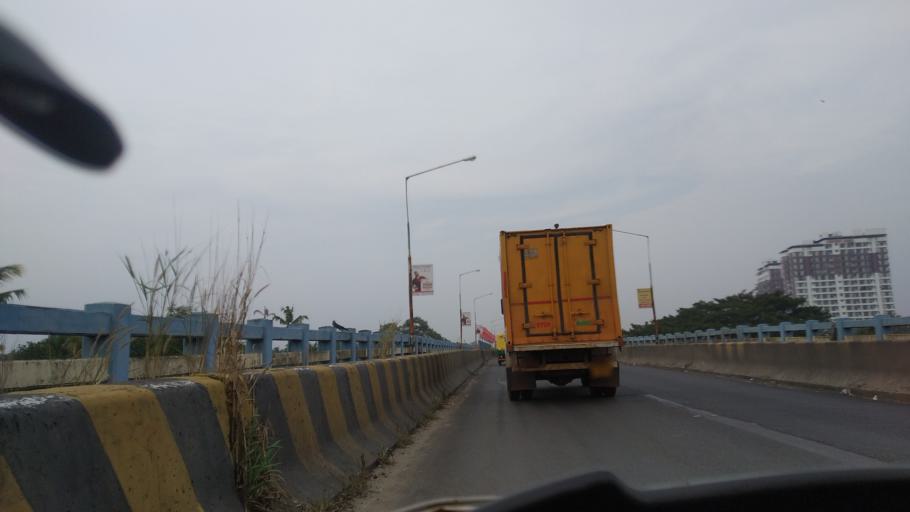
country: IN
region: Kerala
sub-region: Ernakulam
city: Elur
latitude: 10.0349
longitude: 76.3032
